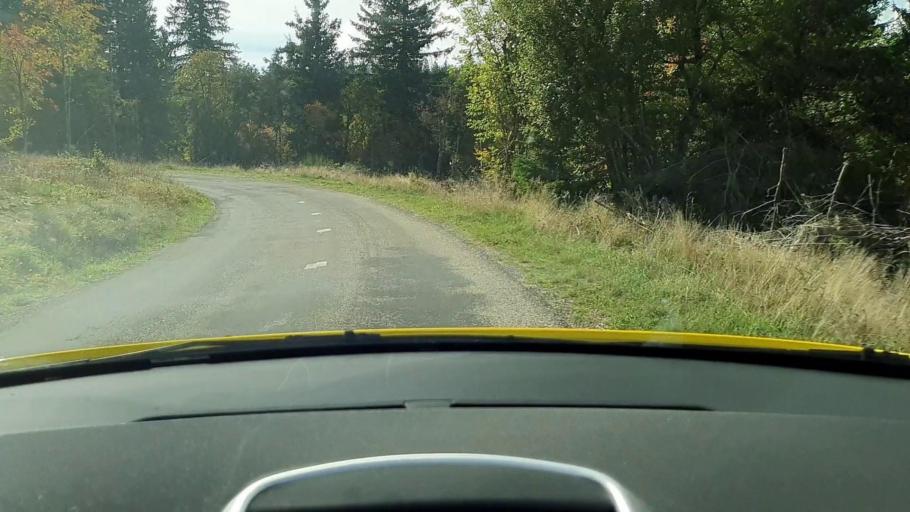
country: FR
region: Languedoc-Roussillon
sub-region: Departement du Gard
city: Valleraugue
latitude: 44.0571
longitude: 3.5712
